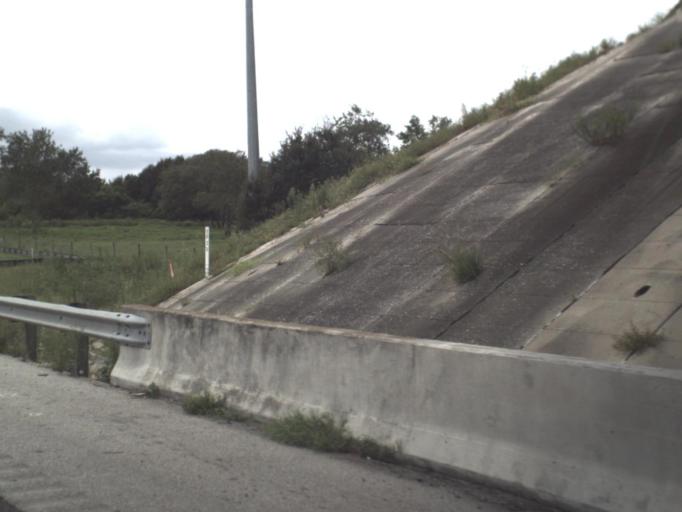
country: US
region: Florida
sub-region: Pasco County
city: Wesley Chapel
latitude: 28.2735
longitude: -82.3274
